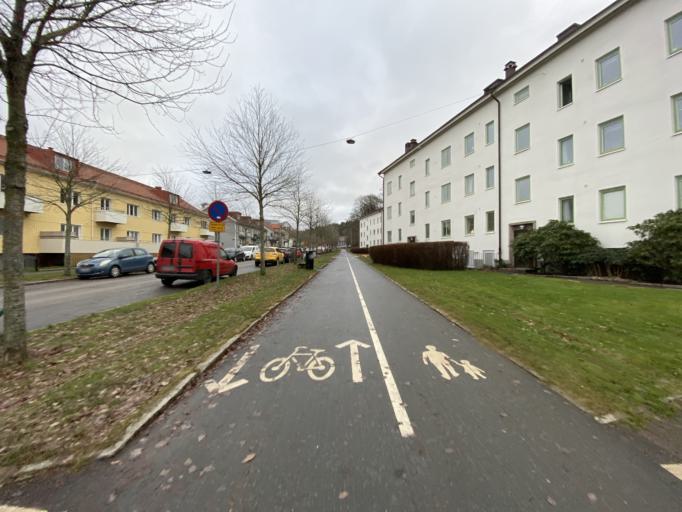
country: SE
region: Vaestra Goetaland
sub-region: Molndal
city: Moelndal
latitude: 57.7110
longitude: 12.0281
